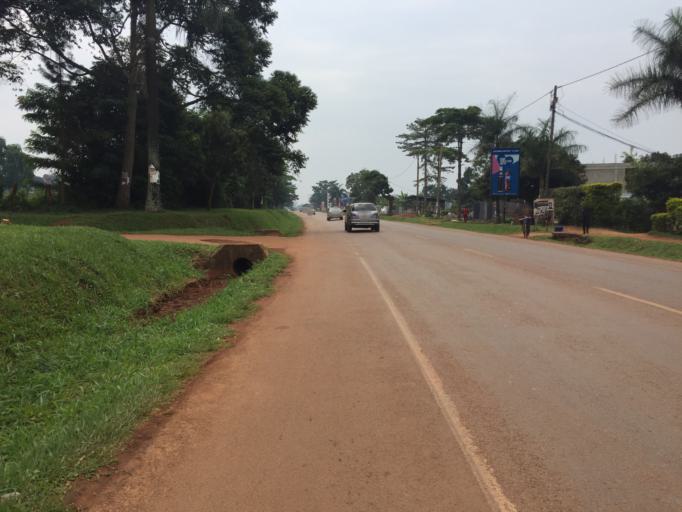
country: UG
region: Central Region
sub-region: Wakiso District
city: Kajansi
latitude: 0.1274
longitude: 32.5313
